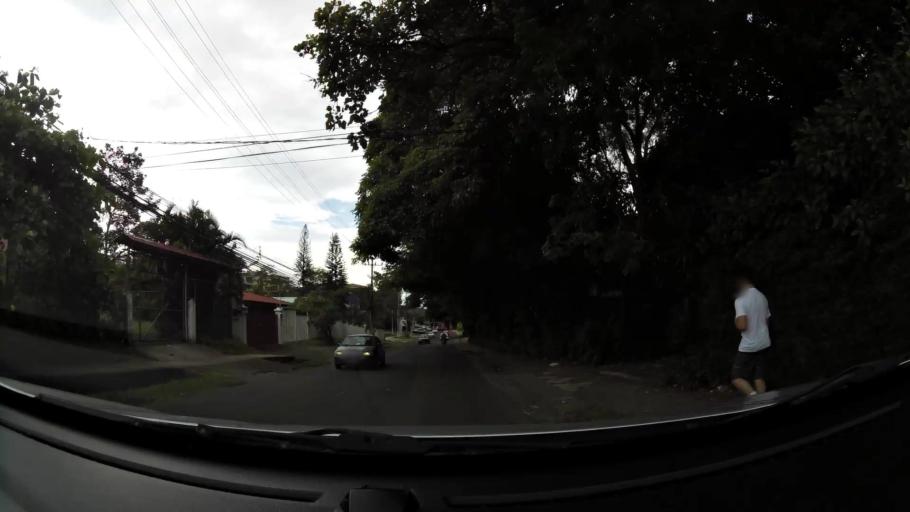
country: CR
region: San Jose
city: San Rafael
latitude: 9.9318
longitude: -84.1517
